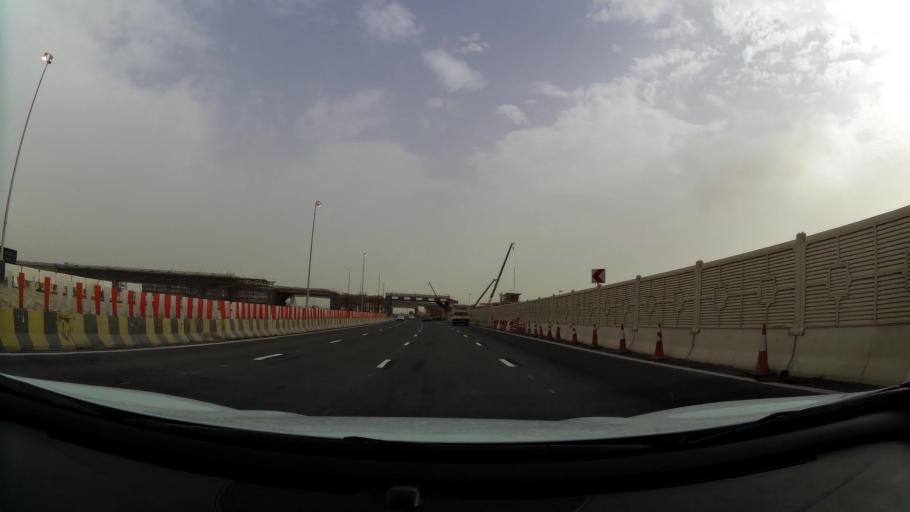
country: AE
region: Abu Dhabi
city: Abu Dhabi
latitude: 24.4544
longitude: 54.6240
